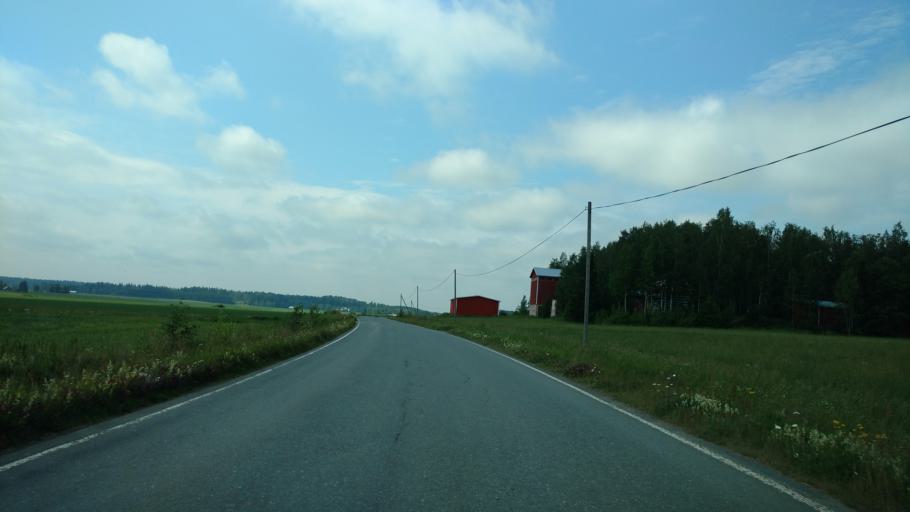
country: FI
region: Haeme
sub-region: Forssa
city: Jokioinen
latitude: 60.7899
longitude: 23.3952
